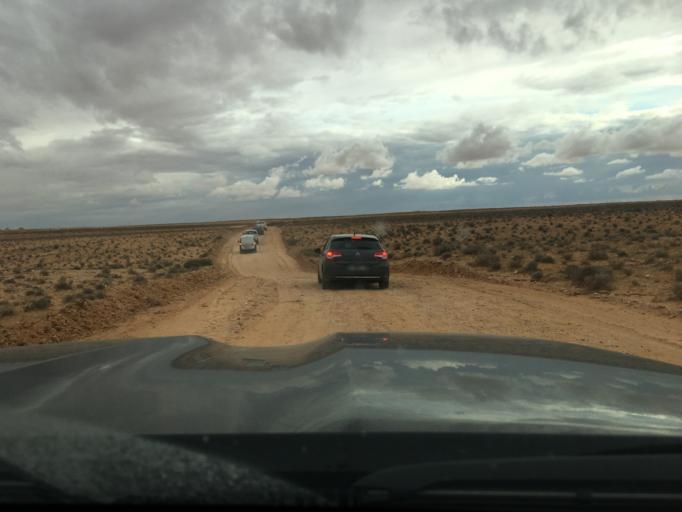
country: TN
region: Madanin
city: Medenine
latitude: 33.2639
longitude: 10.5710
